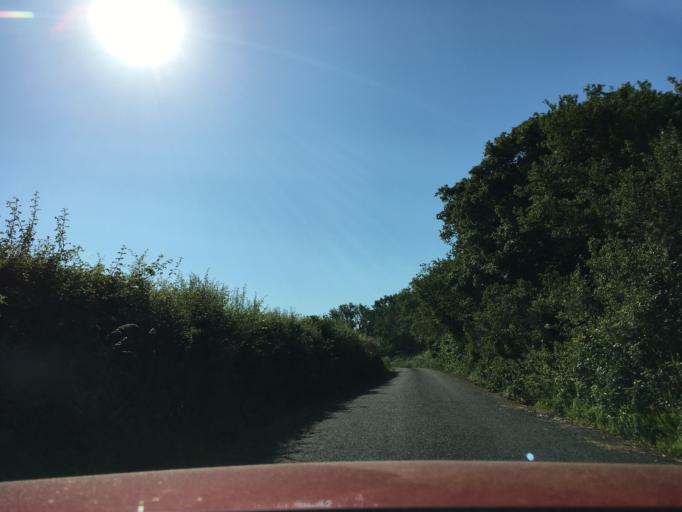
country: GB
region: England
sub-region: South Gloucestershire
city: Hinton
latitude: 51.4783
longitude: -2.3888
